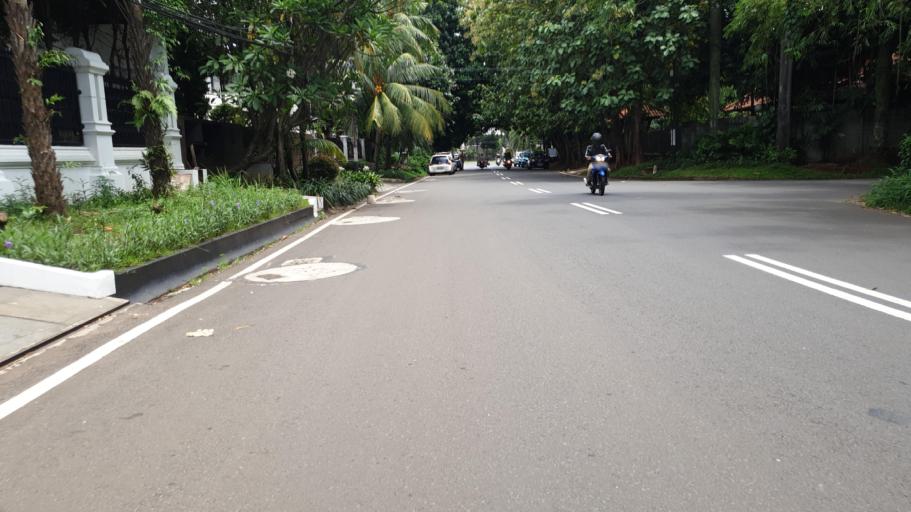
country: ID
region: Banten
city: South Tangerang
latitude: -6.2782
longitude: 106.7853
